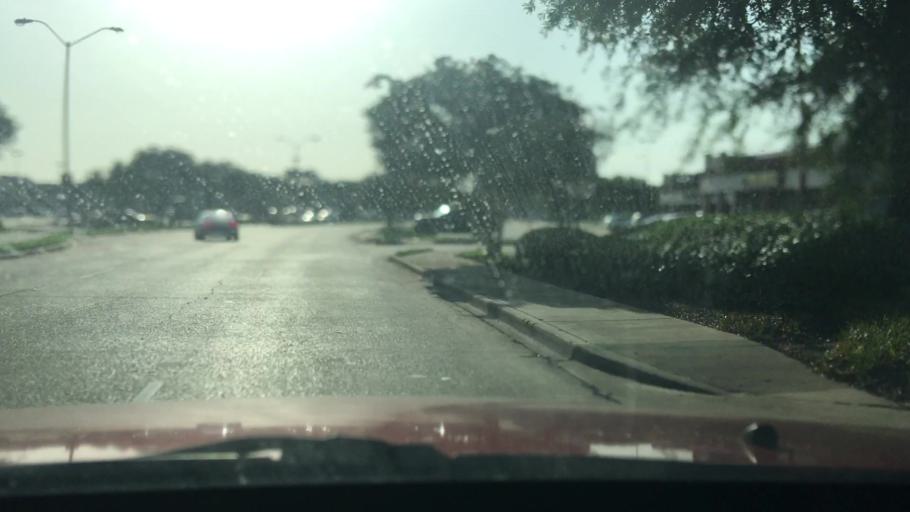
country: US
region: Texas
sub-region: Dallas County
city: Addison
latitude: 32.9833
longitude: -96.8039
